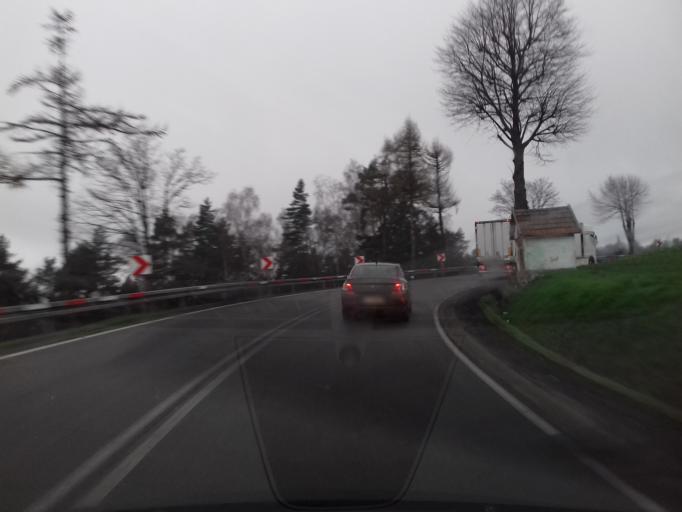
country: PL
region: Lesser Poland Voivodeship
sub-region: Powiat nowosadecki
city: Podegrodzie
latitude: 49.6506
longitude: 20.5757
